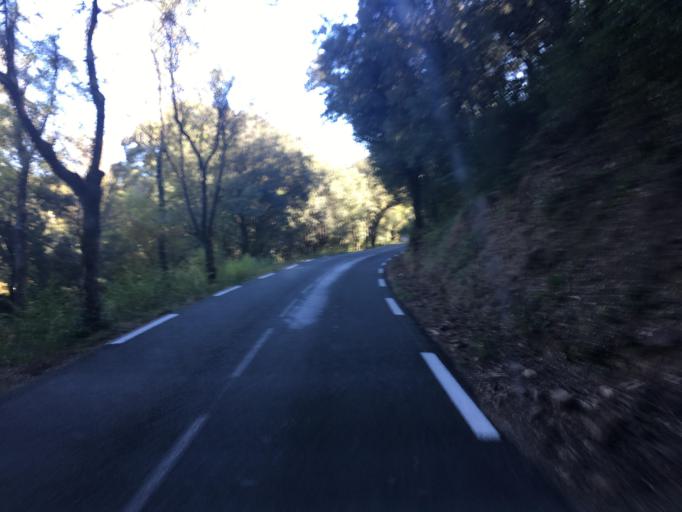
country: FR
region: Languedoc-Roussillon
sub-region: Departement de l'Herault
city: Nebian
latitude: 43.6140
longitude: 3.3783
